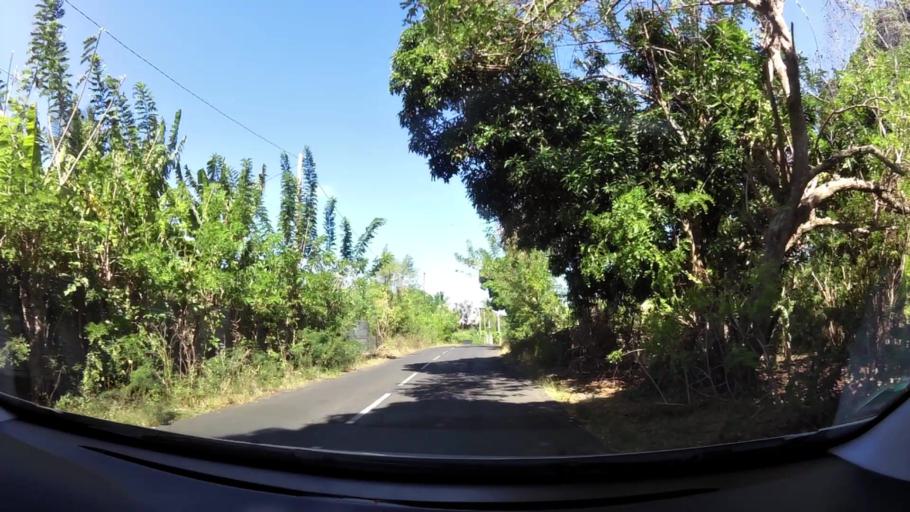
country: YT
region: Pamandzi
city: Pamandzi
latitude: -12.7734
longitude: 45.2806
